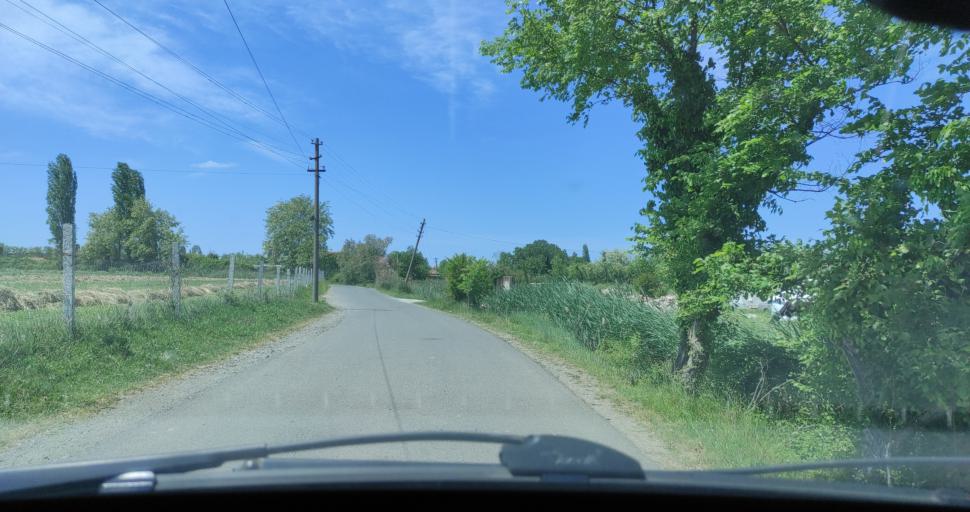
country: AL
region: Lezhe
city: Lezhe
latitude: 41.7566
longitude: 19.6130
